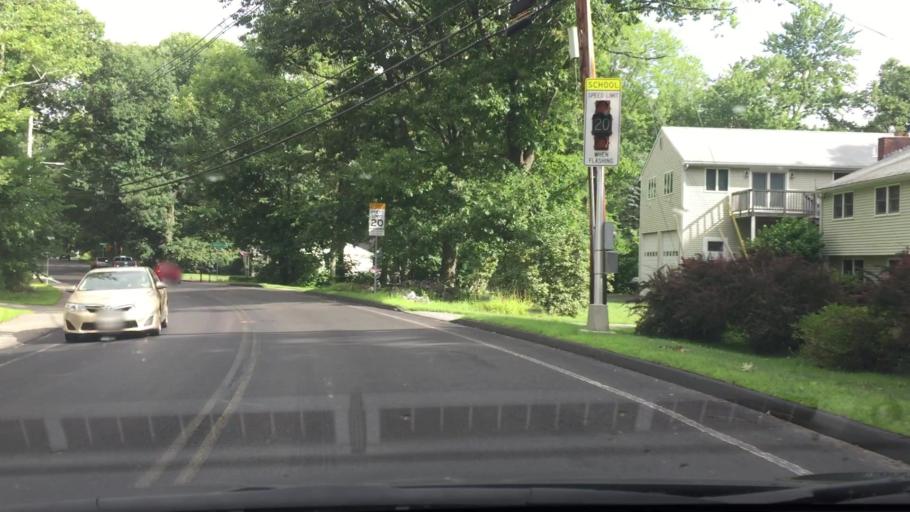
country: US
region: Massachusetts
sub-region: Middlesex County
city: Littleton Common
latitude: 42.5295
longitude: -71.4598
